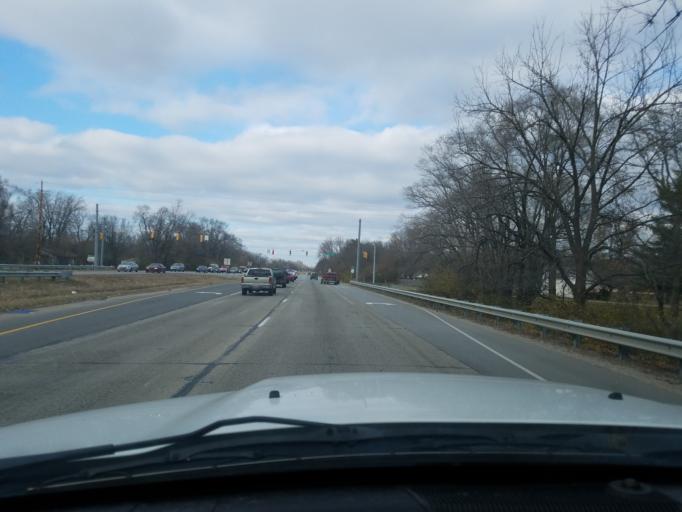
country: US
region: Indiana
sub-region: Marion County
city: Southport
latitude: 39.6408
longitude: -86.2021
